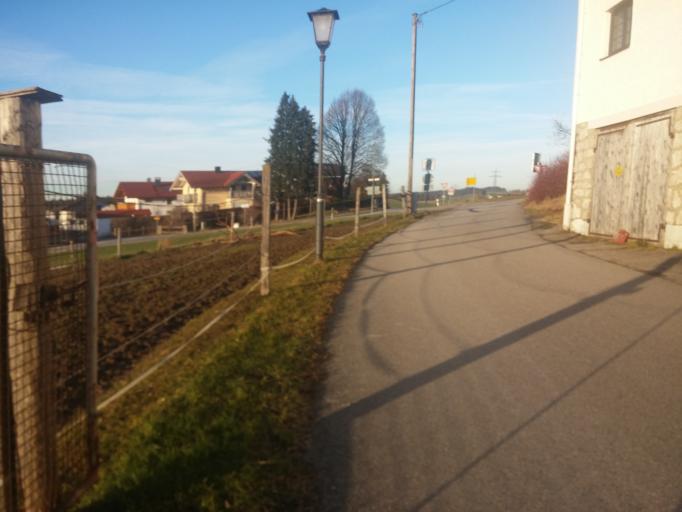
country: DE
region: Bavaria
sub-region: Upper Bavaria
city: Tuntenhausen
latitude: 47.9505
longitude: 12.0346
